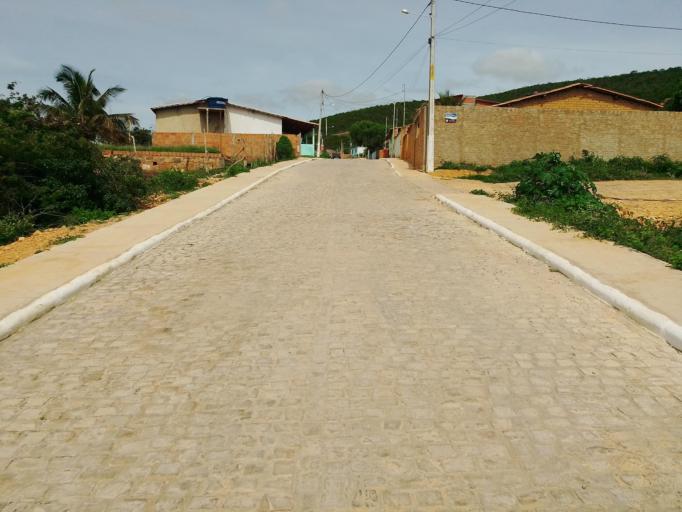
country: BR
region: Bahia
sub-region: Seabra
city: Seabra
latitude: -12.5131
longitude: -41.5779
